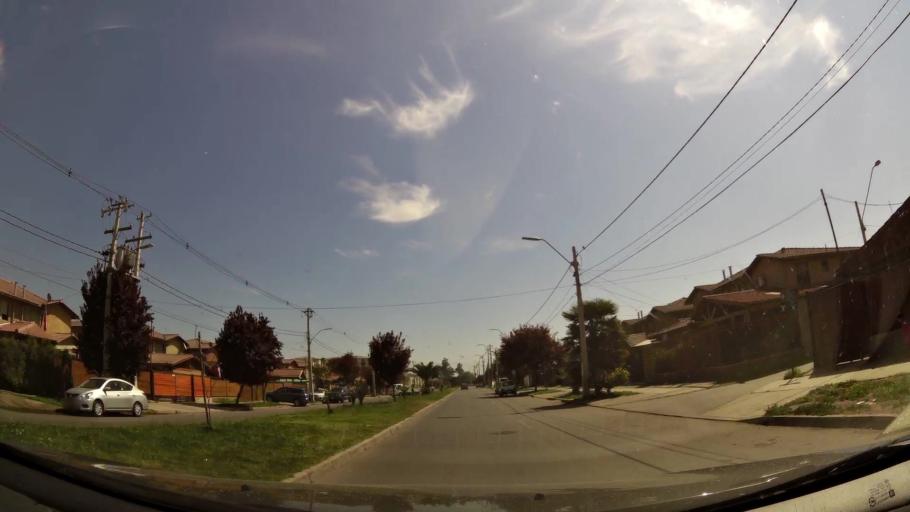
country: CL
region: Santiago Metropolitan
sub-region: Provincia de Santiago
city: Lo Prado
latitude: -33.3952
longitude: -70.7499
